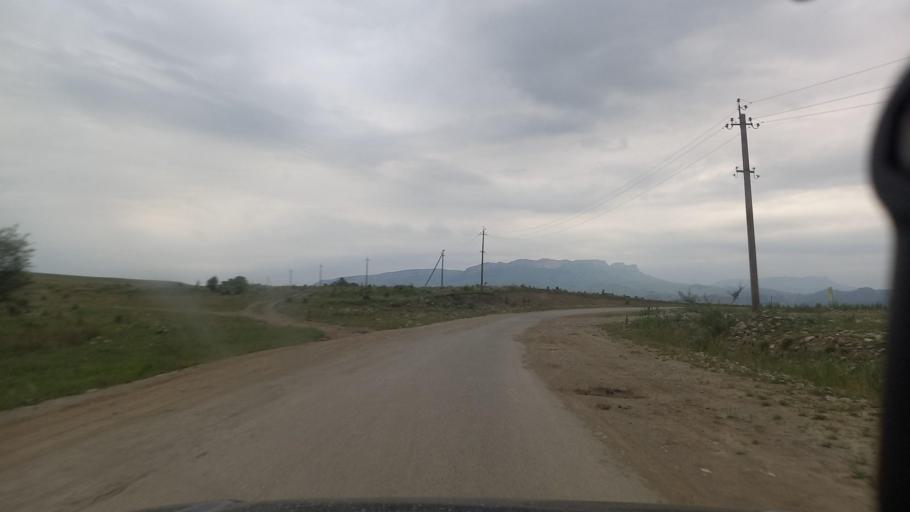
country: RU
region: Karachayevo-Cherkesiya
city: Pregradnaya
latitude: 43.9447
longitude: 41.1582
